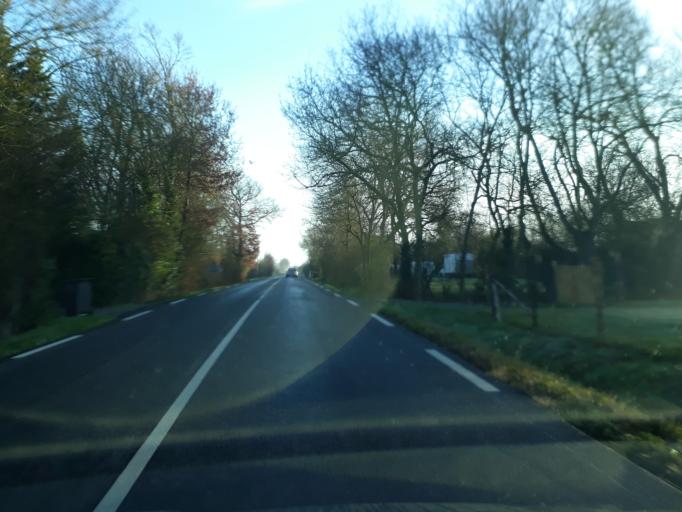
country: FR
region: Midi-Pyrenees
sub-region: Departement de la Haute-Garonne
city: Rieumes
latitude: 43.4201
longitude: 1.1382
